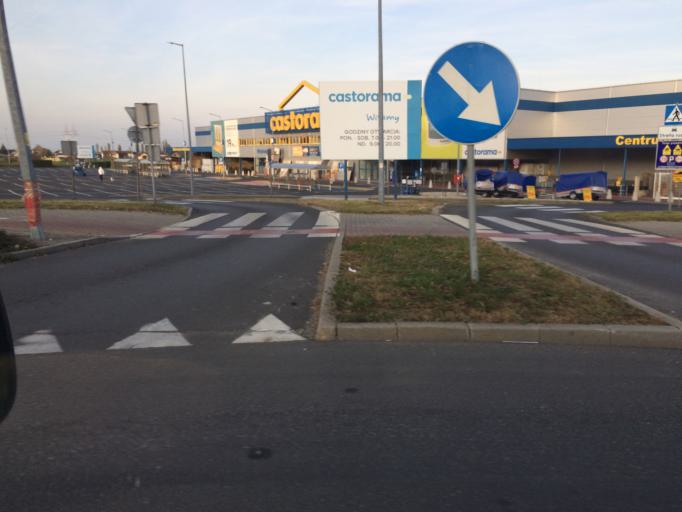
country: PL
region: Opole Voivodeship
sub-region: Powiat opolski
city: Opole
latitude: 50.6746
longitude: 17.9612
